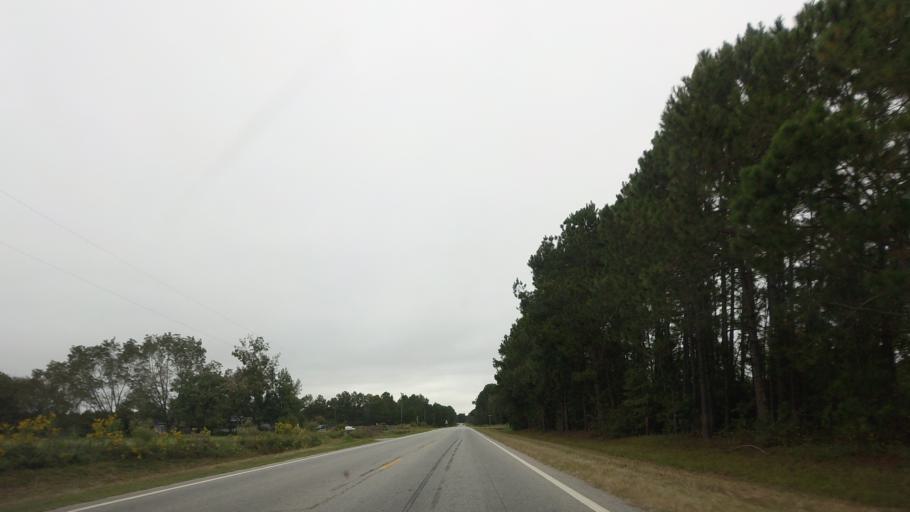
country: US
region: Georgia
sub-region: Berrien County
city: Ray City
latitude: 31.1338
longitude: -83.2154
